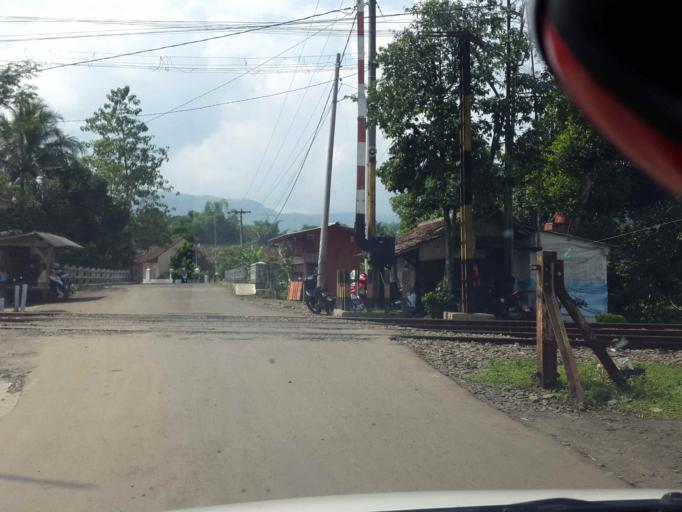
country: ID
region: West Java
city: Cibeber
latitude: -6.9589
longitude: 107.0389
